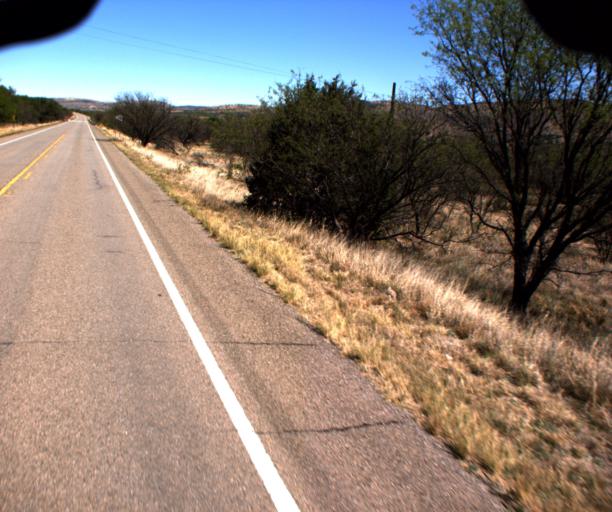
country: US
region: Arizona
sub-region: Santa Cruz County
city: Rio Rico
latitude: 31.5928
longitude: -110.7254
